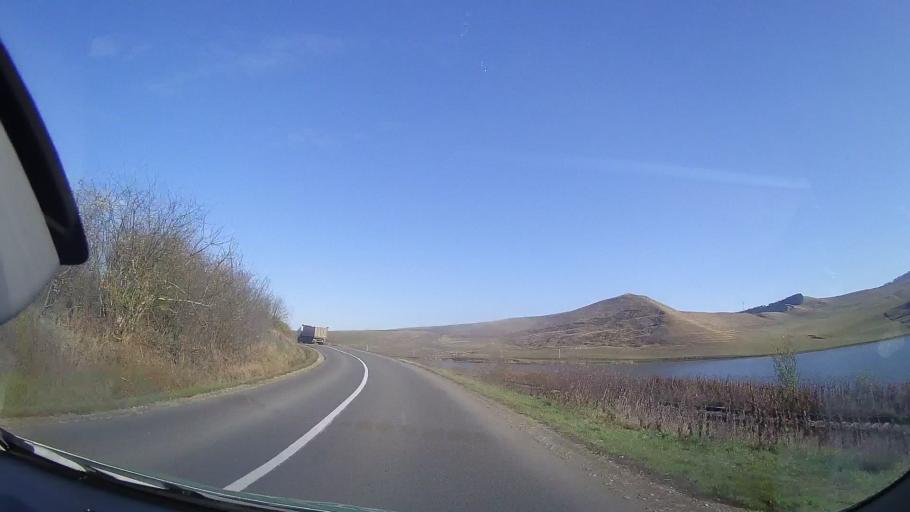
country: RO
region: Mures
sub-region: Comuna Zau De Campie
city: Zau de Campie
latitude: 46.6390
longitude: 24.1431
